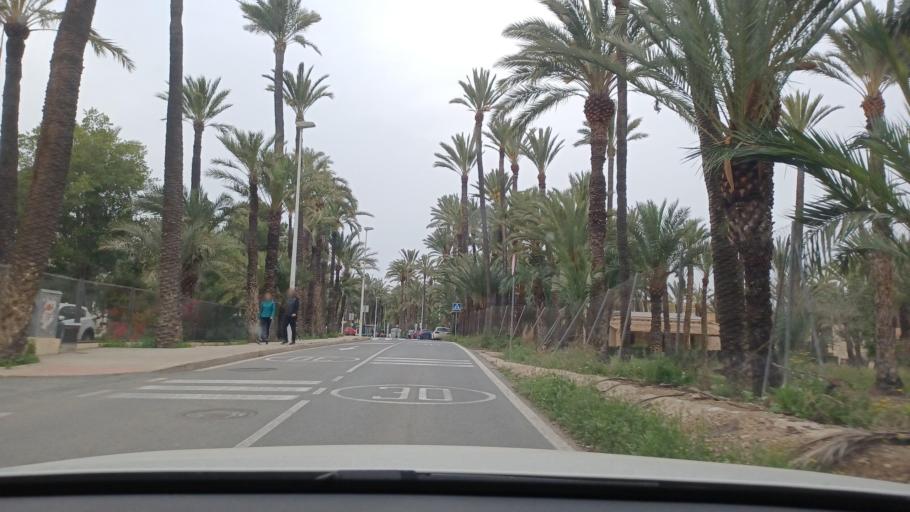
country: ES
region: Valencia
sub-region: Provincia de Alicante
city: Elche
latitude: 38.2557
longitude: -0.6920
